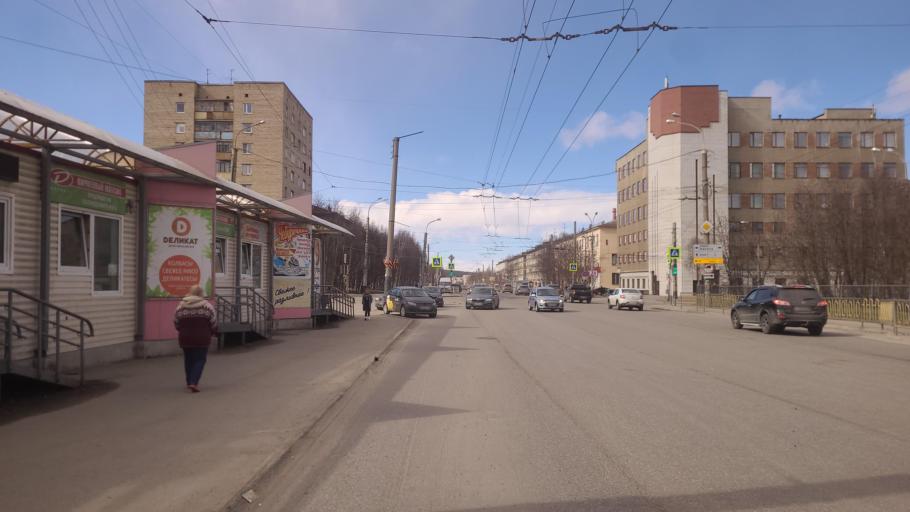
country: RU
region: Murmansk
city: Murmansk
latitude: 68.9509
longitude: 33.0768
